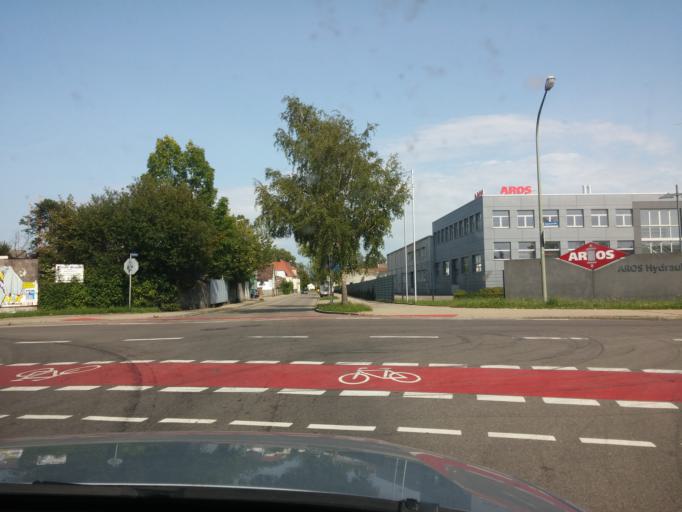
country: DE
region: Bavaria
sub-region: Swabia
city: Memmingen
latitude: 47.9732
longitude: 10.1893
